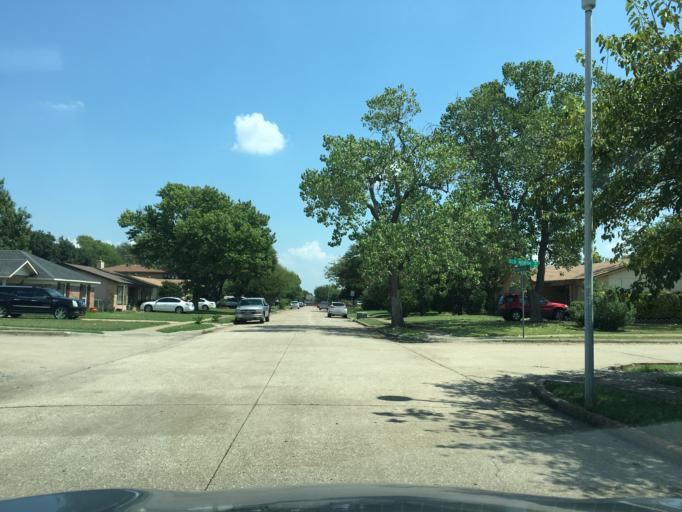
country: US
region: Texas
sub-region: Dallas County
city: Garland
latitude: 32.9382
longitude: -96.6528
